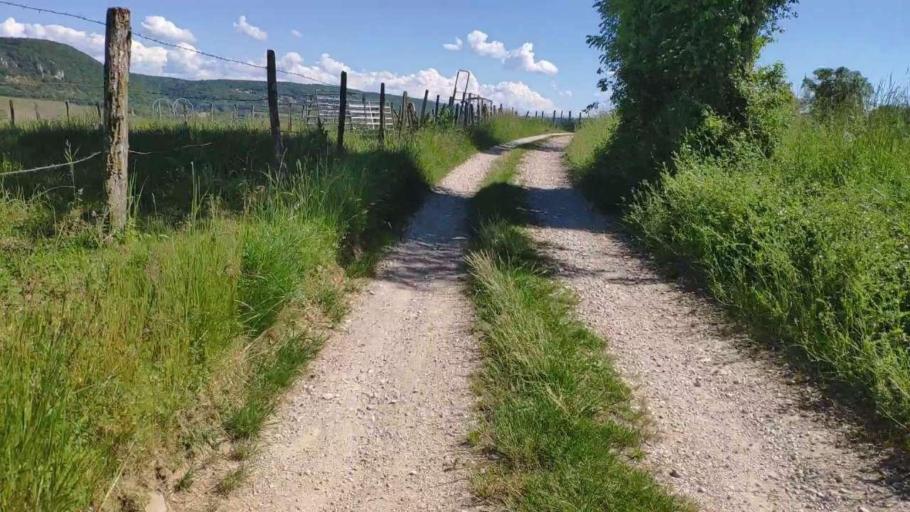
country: FR
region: Franche-Comte
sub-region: Departement du Jura
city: Perrigny
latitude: 46.7236
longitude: 5.5841
